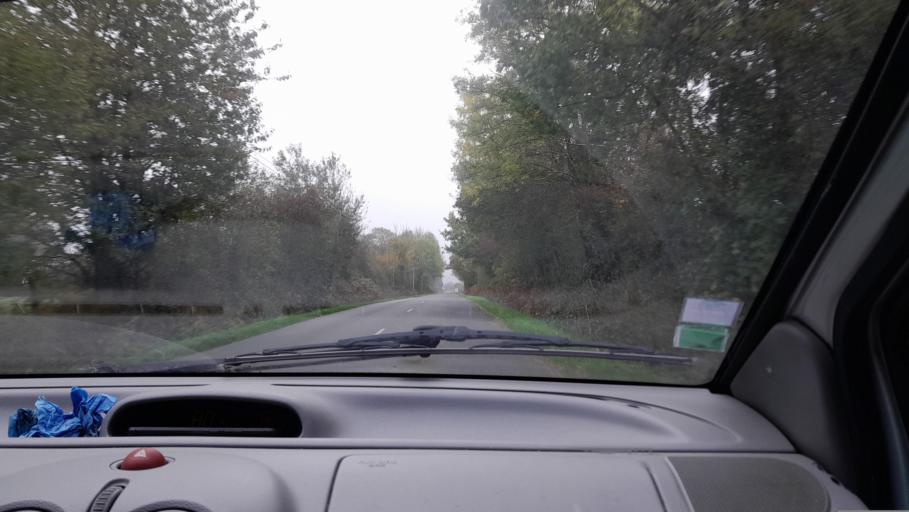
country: FR
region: Pays de la Loire
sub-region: Departement de la Mayenne
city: Saint-Berthevin
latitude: 48.0580
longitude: -0.8506
